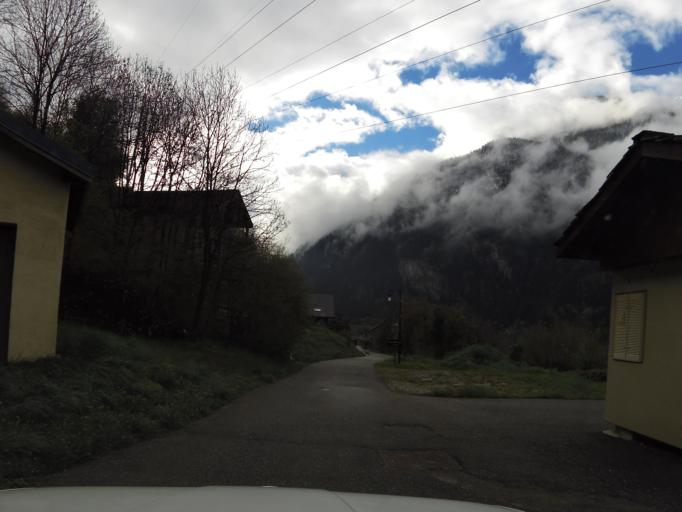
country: FR
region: Rhone-Alpes
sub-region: Departement de la Savoie
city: Saint-Michel-de-Maurienne
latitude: 45.2111
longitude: 6.5527
